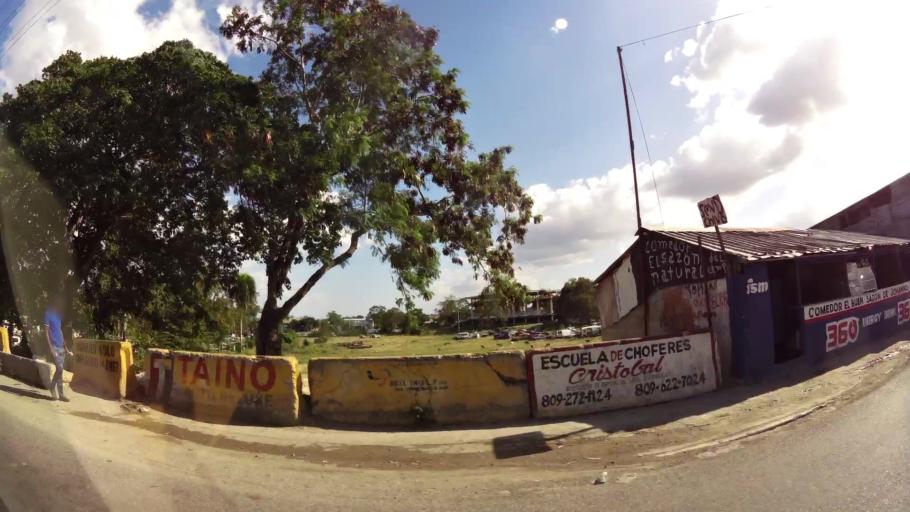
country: DO
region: Nacional
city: Santo Domingo
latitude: 18.5074
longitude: -69.9874
